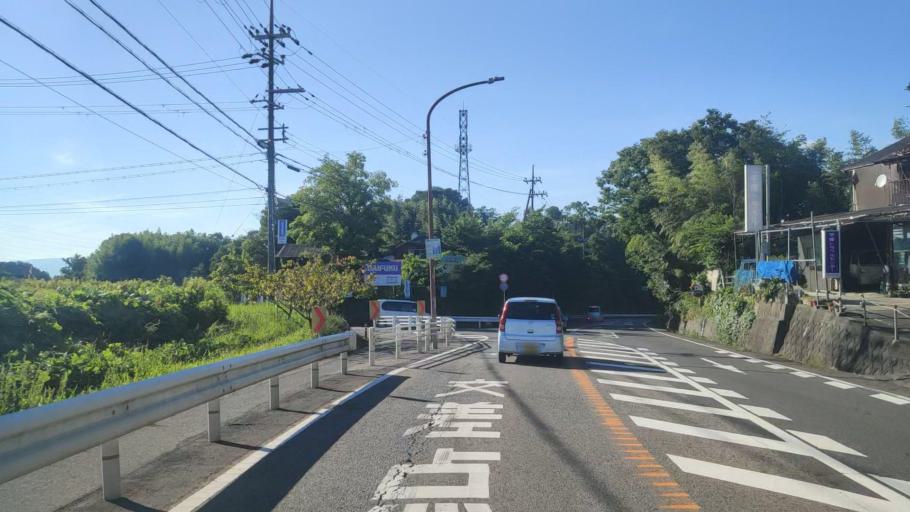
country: JP
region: Shiga Prefecture
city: Hino
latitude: 35.0466
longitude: 136.2389
